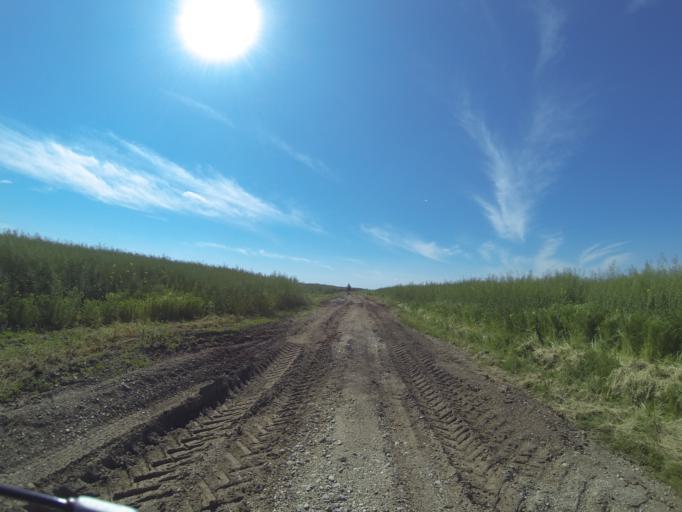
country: RO
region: Dolj
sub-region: Comuna Cosoveni
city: Cosoveni
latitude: 44.2624
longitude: 23.9711
